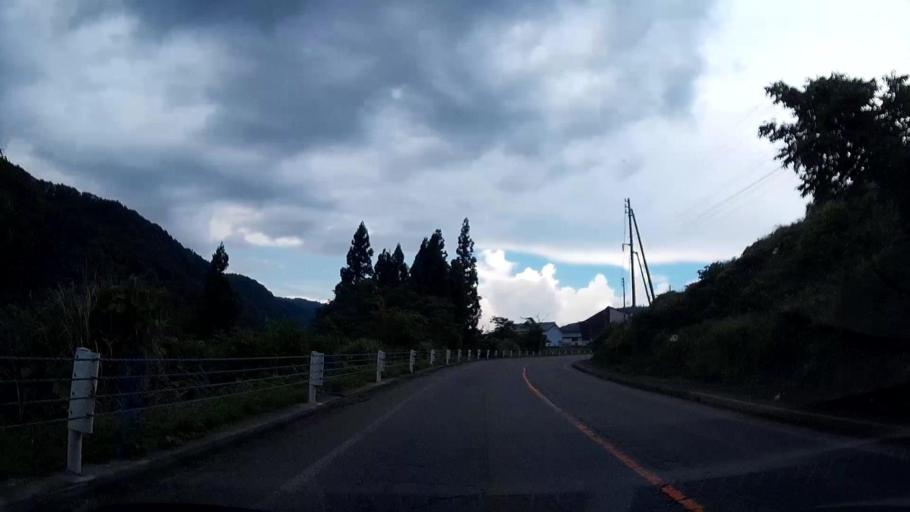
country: JP
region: Nagano
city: Iiyama
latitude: 36.9846
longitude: 138.5138
